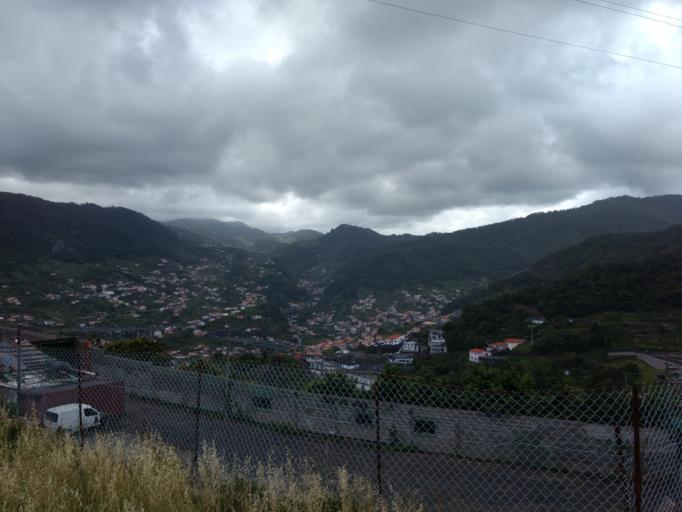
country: PT
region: Madeira
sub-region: Machico
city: Canical
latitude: 32.7299
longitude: -16.7630
